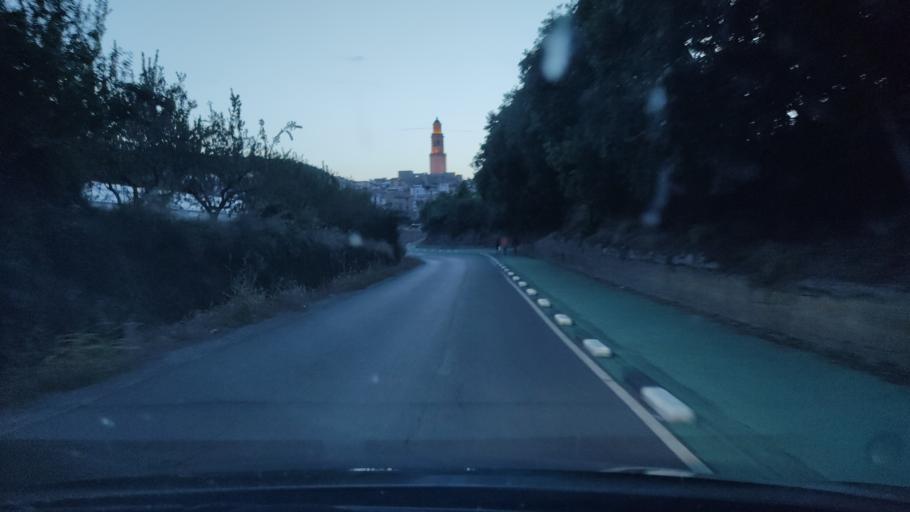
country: ES
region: Valencia
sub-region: Provincia de Castello
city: Jerica
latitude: 39.9099
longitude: -0.5659
